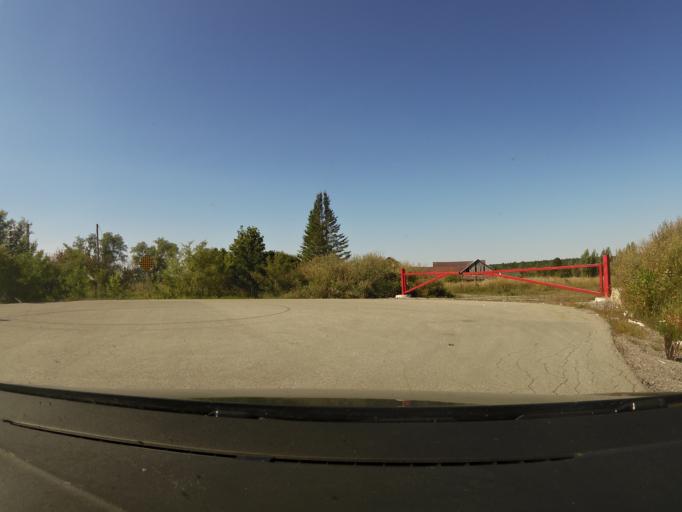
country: CA
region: Ontario
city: Bells Corners
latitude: 45.2337
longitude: -75.9904
